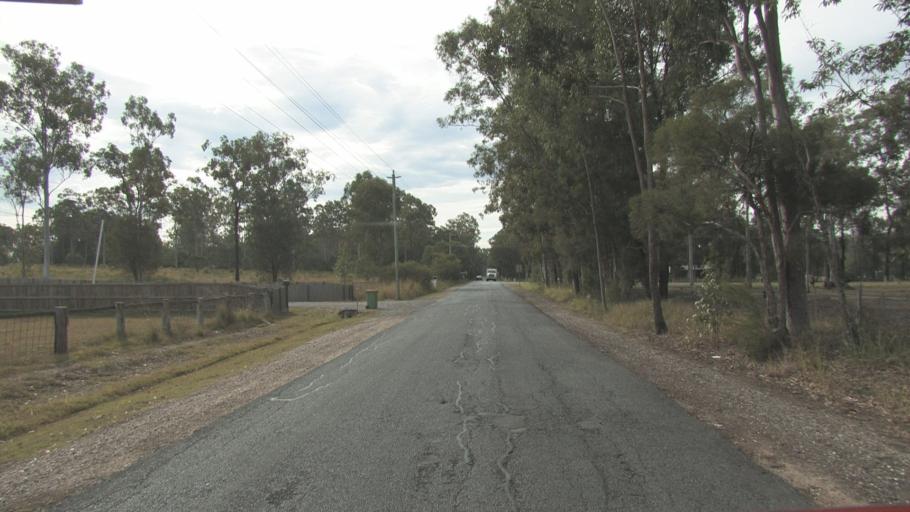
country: AU
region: Queensland
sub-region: Logan
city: Chambers Flat
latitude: -27.7716
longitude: 153.1159
